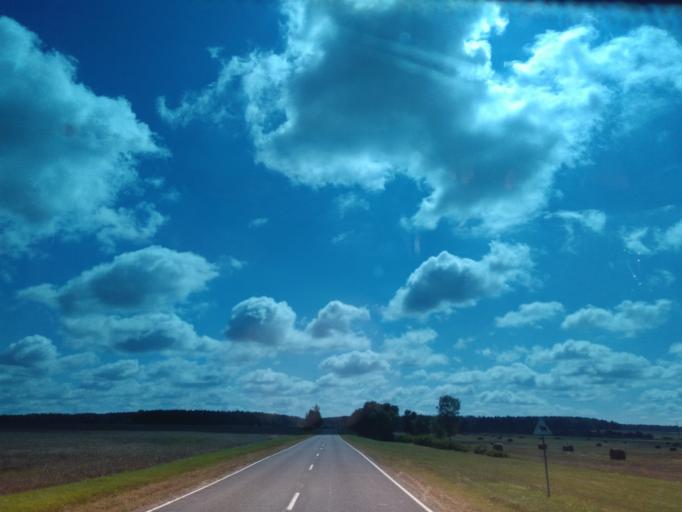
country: BY
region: Minsk
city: Uzda
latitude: 53.3934
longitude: 27.2362
